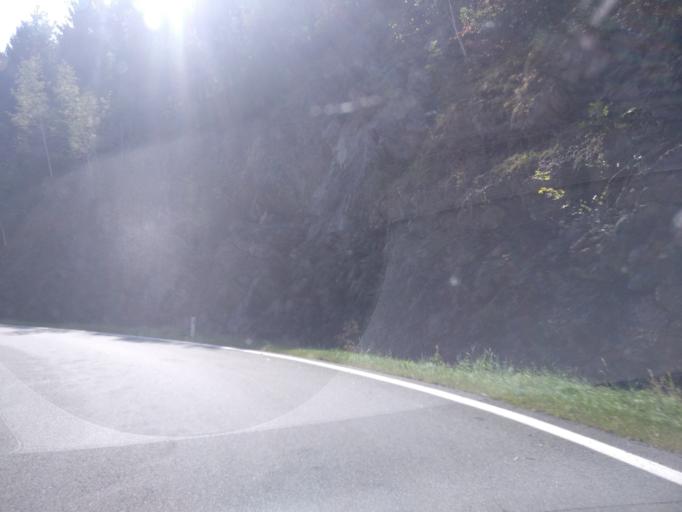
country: AT
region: Salzburg
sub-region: Politischer Bezirk Sankt Johann im Pongau
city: Bischofshofen
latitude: 47.4076
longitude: 13.2122
